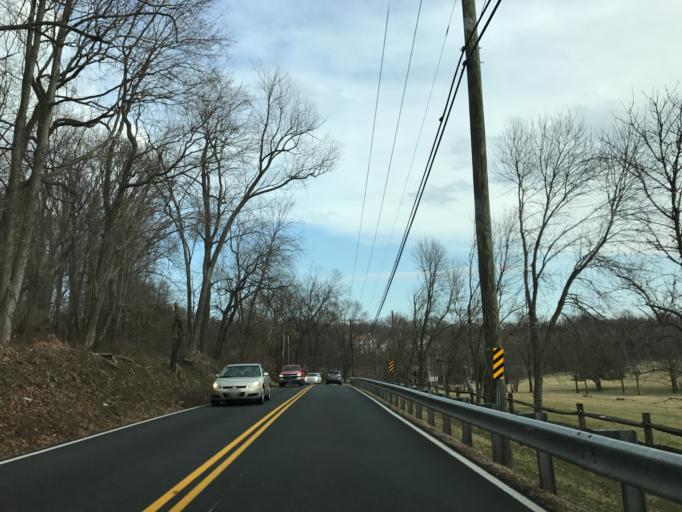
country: US
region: Maryland
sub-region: Harford County
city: North Bel Air
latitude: 39.5279
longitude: -76.3716
